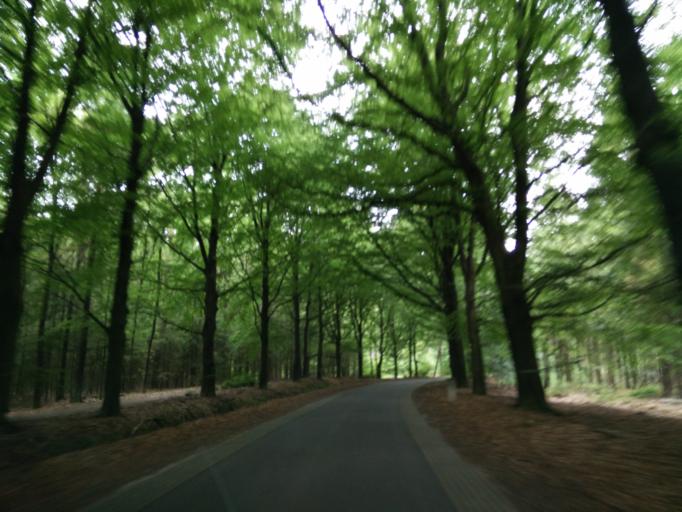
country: NL
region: Drenthe
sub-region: Gemeente Borger-Odoorn
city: Borger
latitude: 52.9479
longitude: 6.7247
